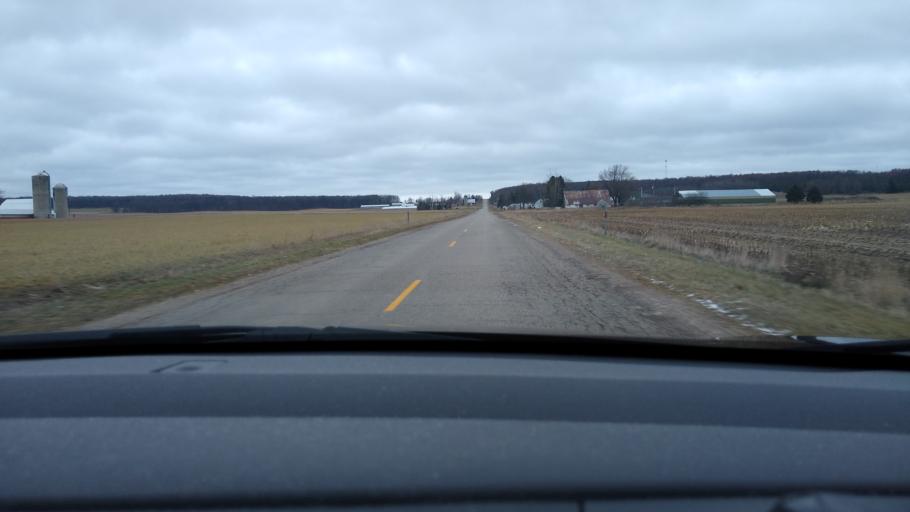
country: US
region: Michigan
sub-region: Missaukee County
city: Lake City
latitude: 44.2756
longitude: -85.0540
